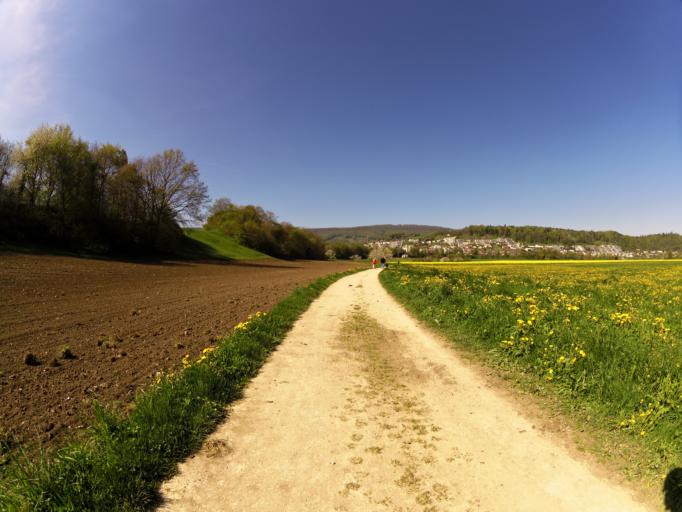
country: CH
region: Solothurn
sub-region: Bezirk Goesgen
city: Niedererlinsbach
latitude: 47.3883
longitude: 8.0136
